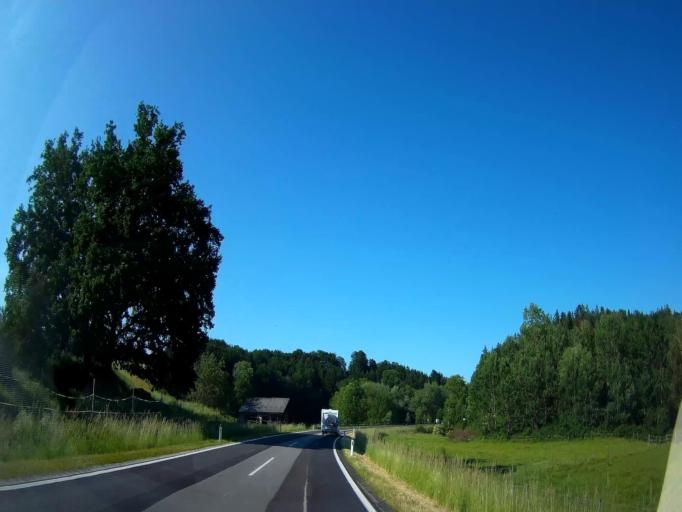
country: AT
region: Salzburg
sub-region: Politischer Bezirk Salzburg-Umgebung
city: Dorfbeuern
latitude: 48.1298
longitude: 13.0115
